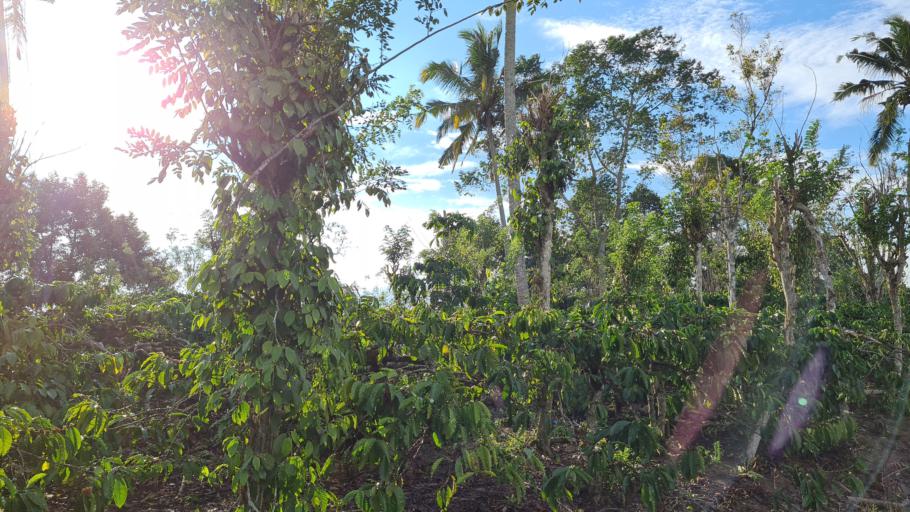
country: ID
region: Lampung
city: Kenali
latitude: -5.0606
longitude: 104.4105
